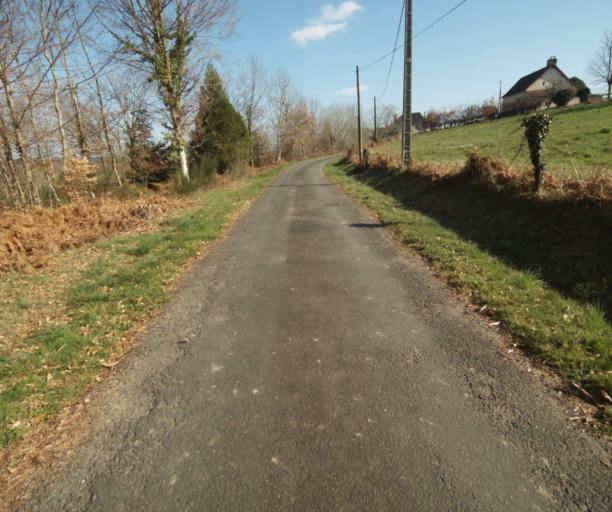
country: FR
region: Limousin
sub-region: Departement de la Correze
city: Saint-Mexant
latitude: 45.3169
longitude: 1.6238
